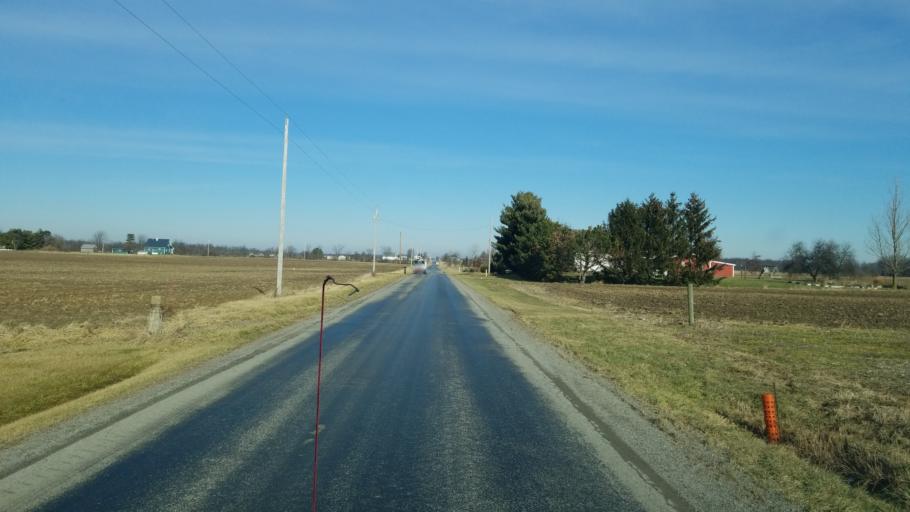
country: US
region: Ohio
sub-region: Hardin County
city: Ada
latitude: 40.8088
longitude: -83.8800
